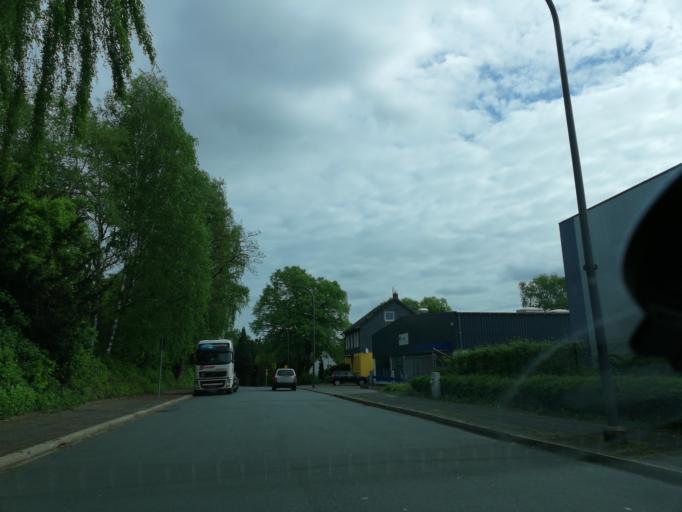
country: DE
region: North Rhine-Westphalia
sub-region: Regierungsbezirk Arnsberg
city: Schwelm
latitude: 51.2963
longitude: 7.2543
